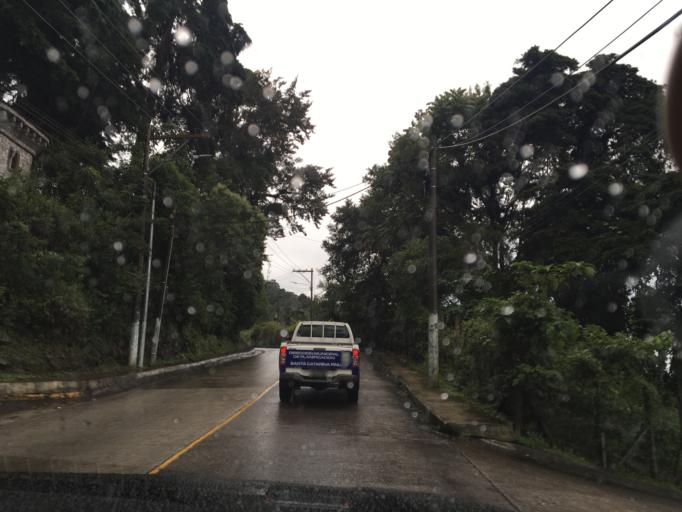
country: GT
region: Guatemala
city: Santa Catarina Pinula
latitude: 14.5566
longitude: -90.4912
